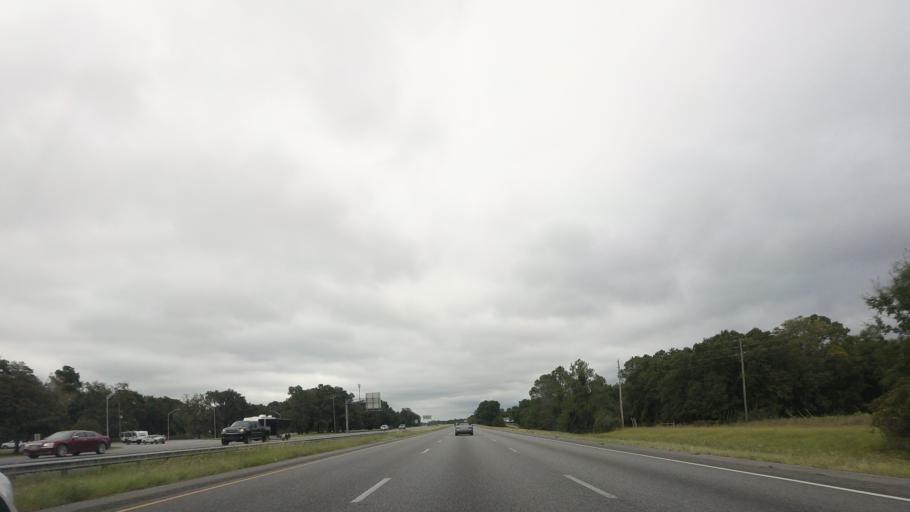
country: US
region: Georgia
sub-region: Lowndes County
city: Valdosta
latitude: 30.6651
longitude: -83.2098
